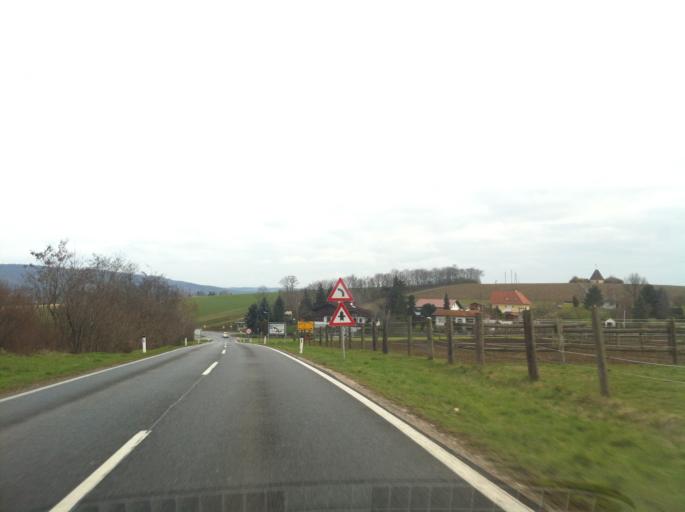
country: AT
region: Lower Austria
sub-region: Politischer Bezirk Tulln
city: Tulln
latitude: 48.2729
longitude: 16.0693
